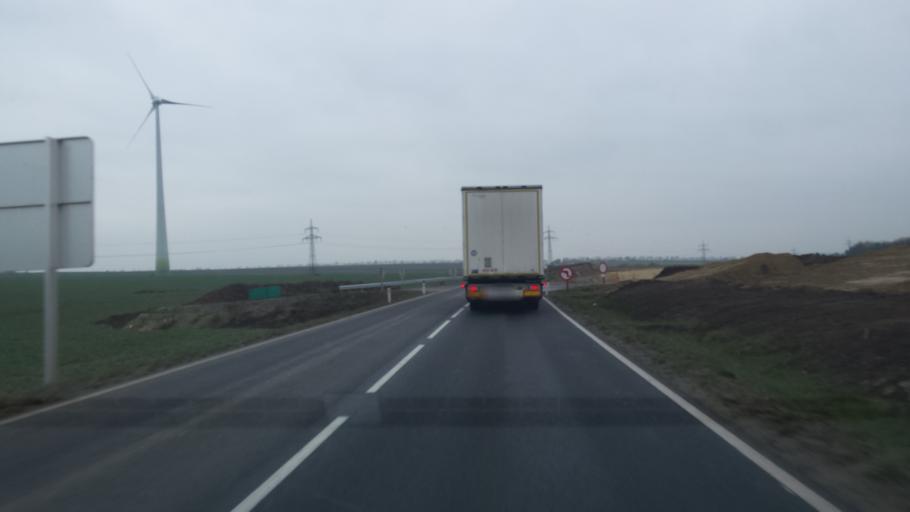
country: AT
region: Lower Austria
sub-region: Politischer Bezirk Mistelbach
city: Wilfersdorf
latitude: 48.5433
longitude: 16.6272
